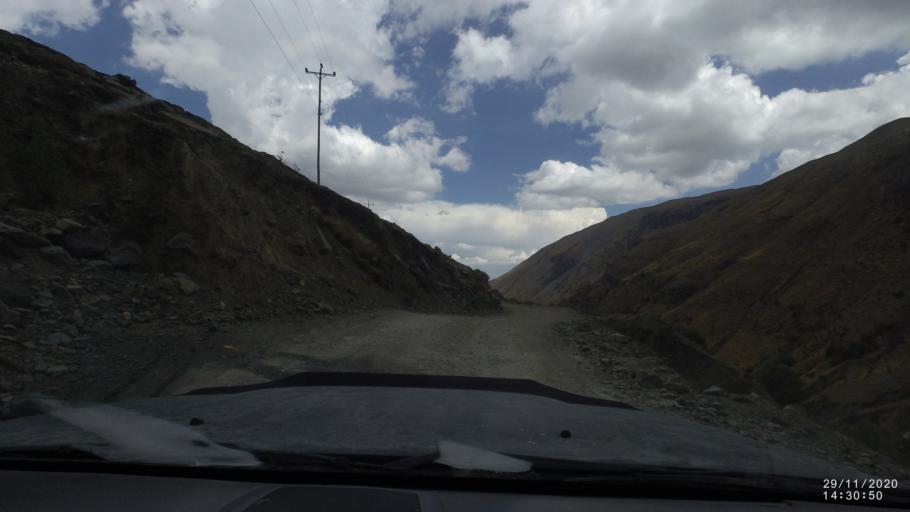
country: BO
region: Cochabamba
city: Sipe Sipe
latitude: -17.2647
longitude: -66.3467
